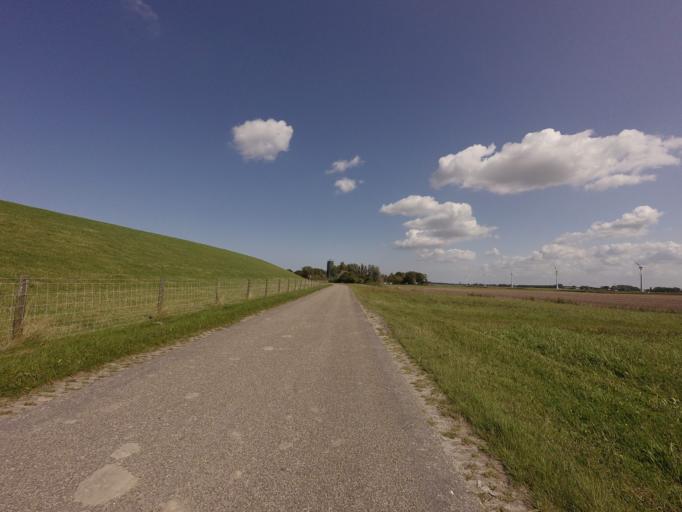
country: NL
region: Friesland
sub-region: Gemeente Ferwerderadiel
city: Hallum
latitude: 53.3264
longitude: 5.7692
